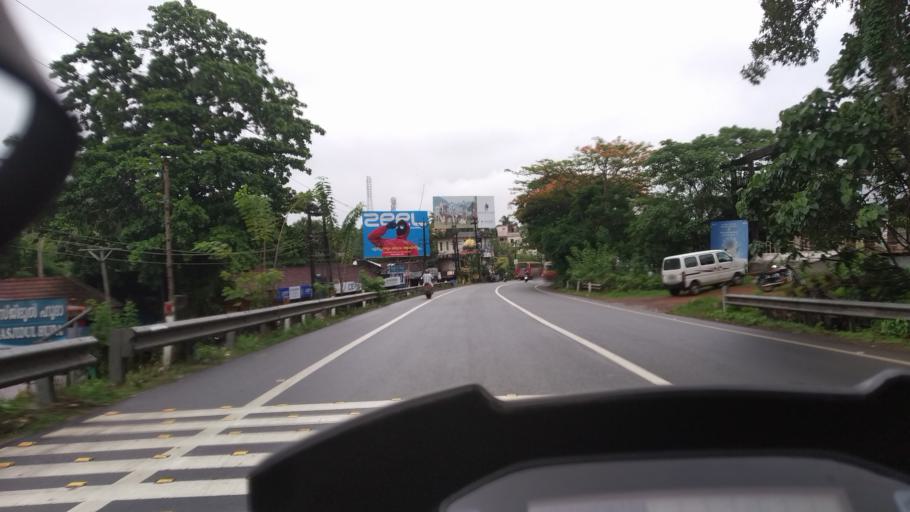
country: IN
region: Kerala
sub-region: Alappuzha
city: Mavelikara
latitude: 9.2829
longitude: 76.4423
